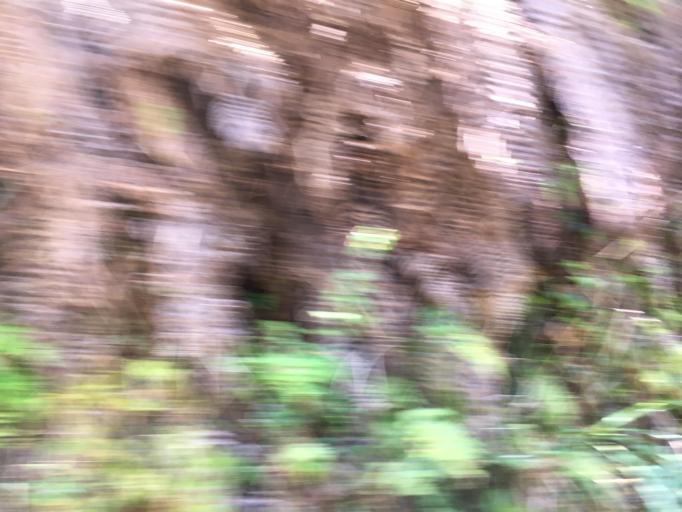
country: TW
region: Taiwan
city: Daxi
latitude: 24.5363
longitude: 121.4020
